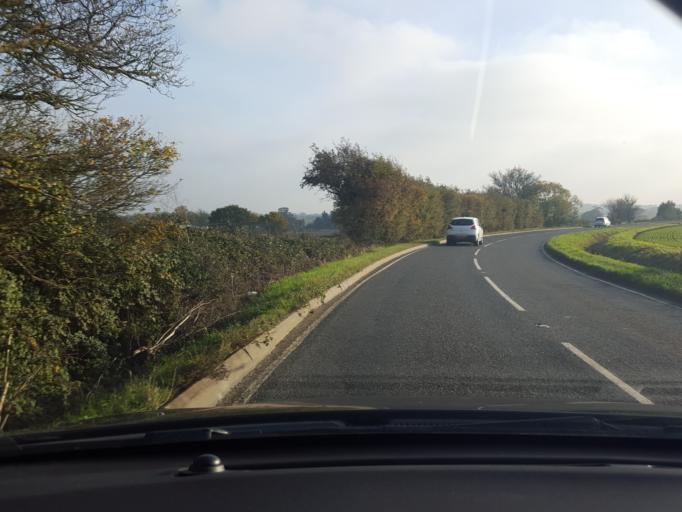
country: GB
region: England
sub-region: Essex
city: Little Clacton
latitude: 51.8760
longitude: 1.1732
